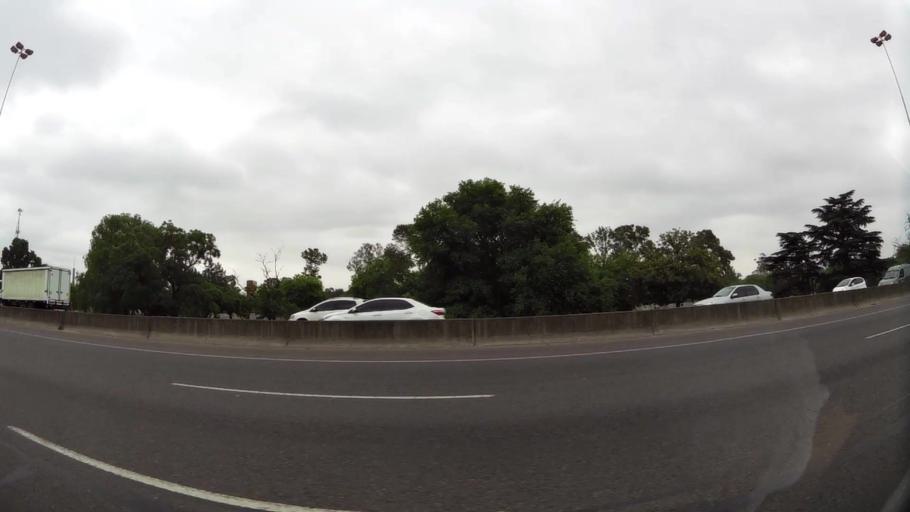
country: AR
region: Buenos Aires
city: San Justo
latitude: -34.7433
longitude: -58.5210
